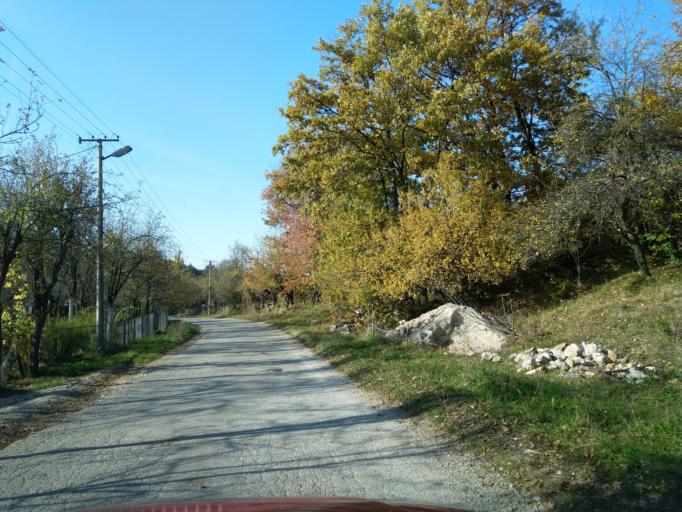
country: RS
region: Central Serbia
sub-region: Zlatiborski Okrug
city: Uzice
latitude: 43.8697
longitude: 19.7573
